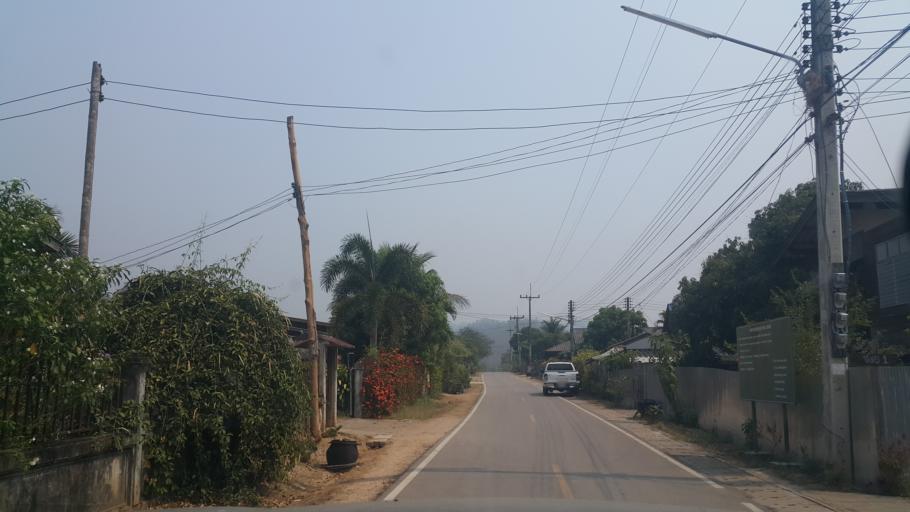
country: TH
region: Lampang
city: Thoen
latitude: 17.7577
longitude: 99.2301
